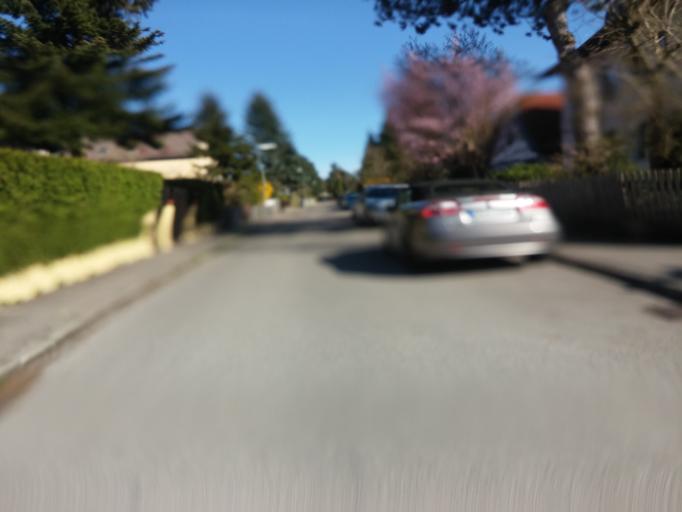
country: DE
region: Bavaria
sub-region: Upper Bavaria
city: Neubiberg
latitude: 48.0797
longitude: 11.6682
